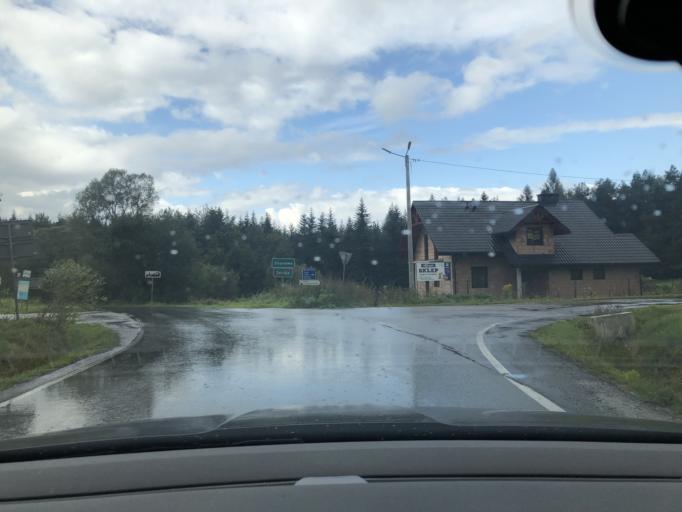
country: PL
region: Lesser Poland Voivodeship
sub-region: Powiat suski
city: Zawoja
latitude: 49.6858
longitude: 19.5637
